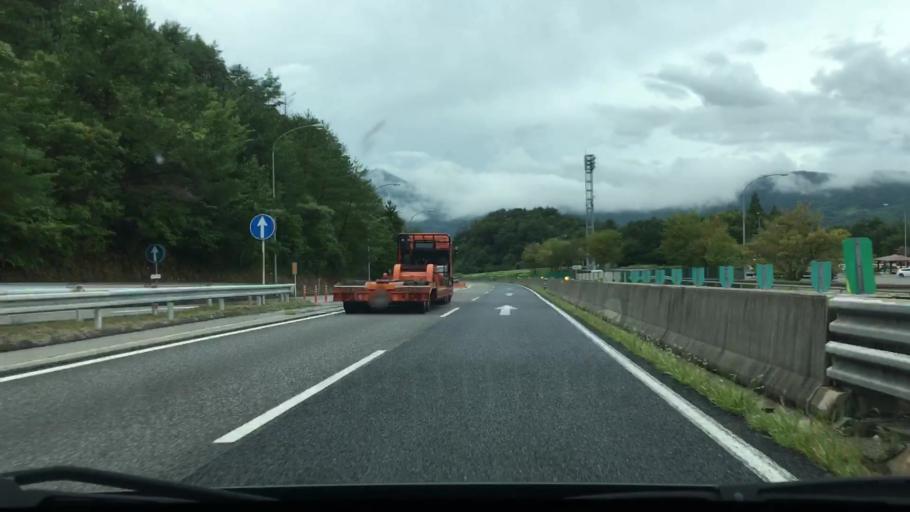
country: JP
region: Hiroshima
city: Hiroshima-shi
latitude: 34.5867
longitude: 132.4796
